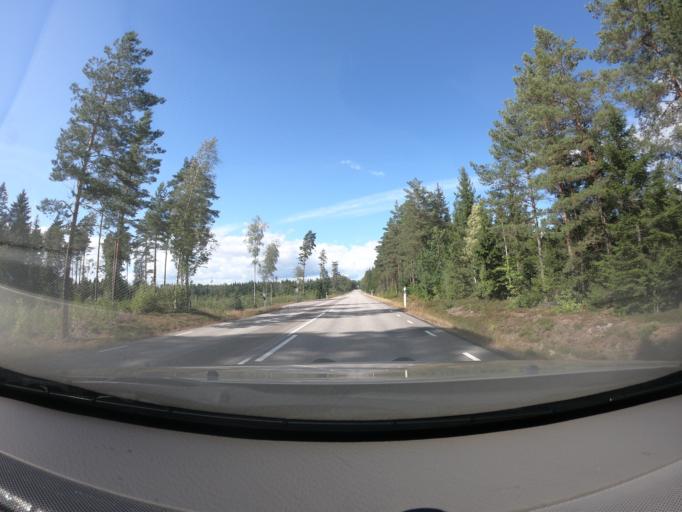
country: SE
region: Kronoberg
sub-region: Vaxjo Kommun
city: Braas
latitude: 57.0422
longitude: 15.0646
